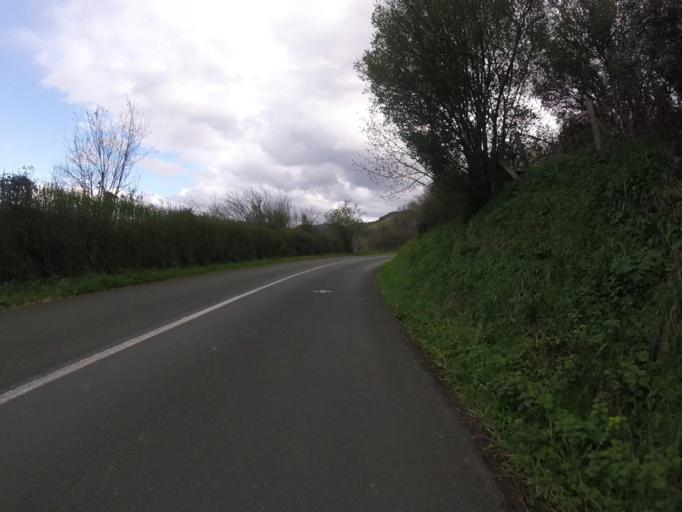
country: ES
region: Basque Country
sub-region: Provincia de Guipuzcoa
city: Errenteria
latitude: 43.2840
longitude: -1.8559
